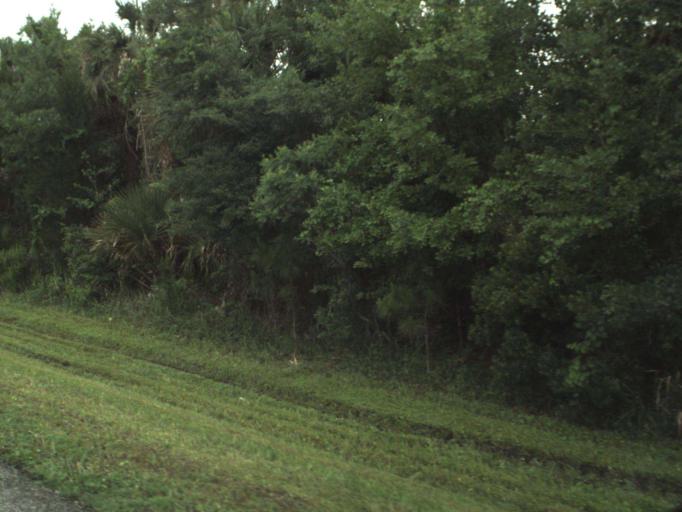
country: US
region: Florida
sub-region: Seminole County
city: Geneva
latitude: 28.6833
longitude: -80.9870
